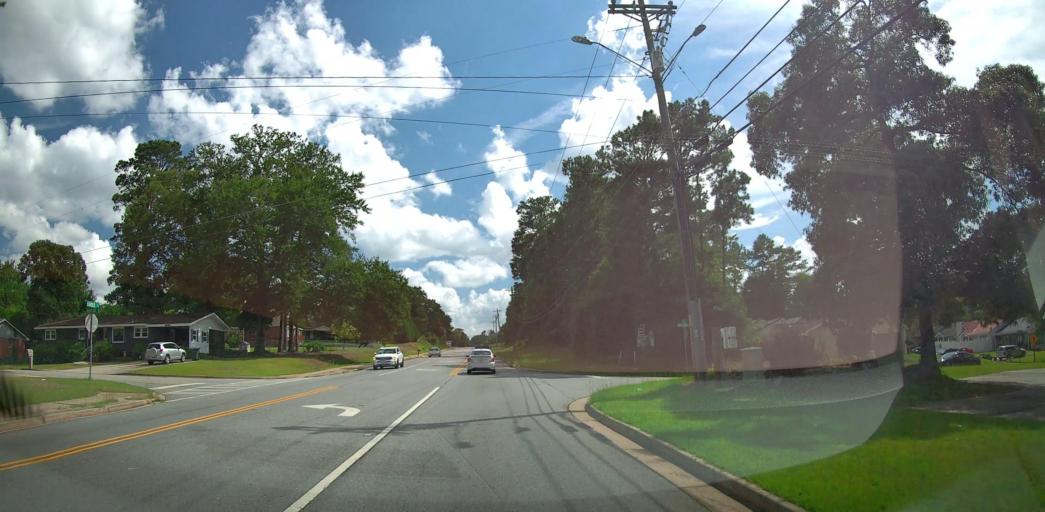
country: US
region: Georgia
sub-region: Houston County
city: Centerville
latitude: 32.6118
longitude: -83.6533
